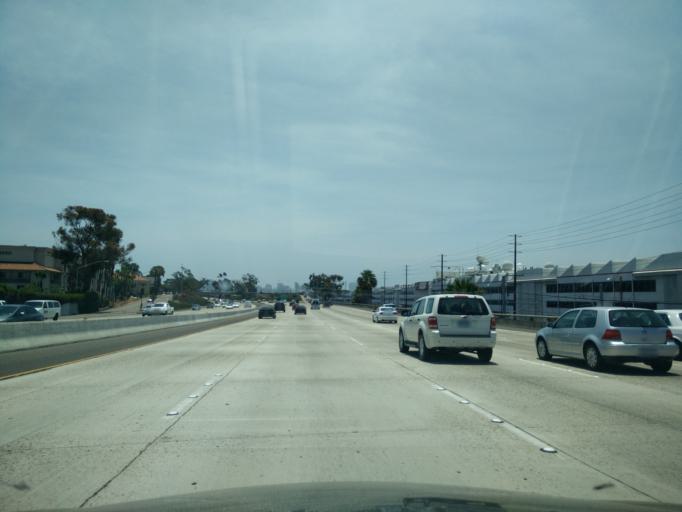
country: US
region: California
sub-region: San Diego County
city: San Diego
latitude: 32.7509
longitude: -117.1970
